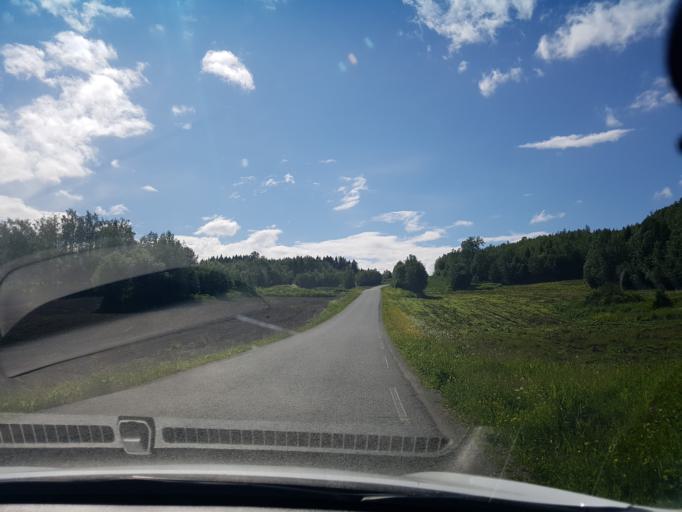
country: NO
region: Nord-Trondelag
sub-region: Frosta
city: Frosta
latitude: 63.6048
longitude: 10.8319
